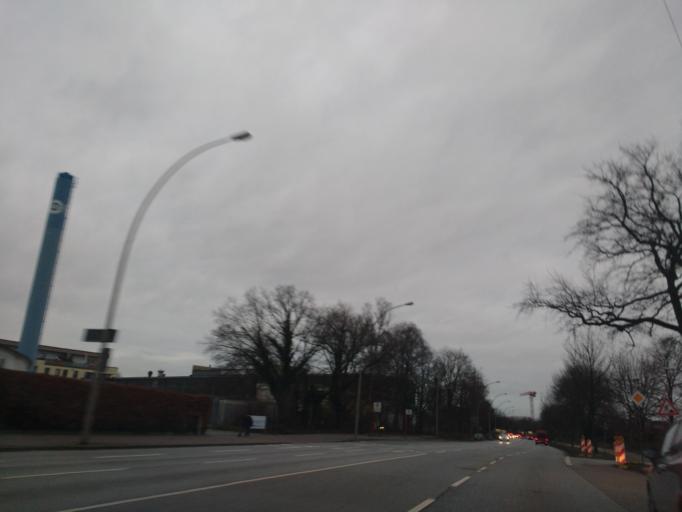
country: DE
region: Hamburg
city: Eidelstedt
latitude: 53.5888
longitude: 9.8766
